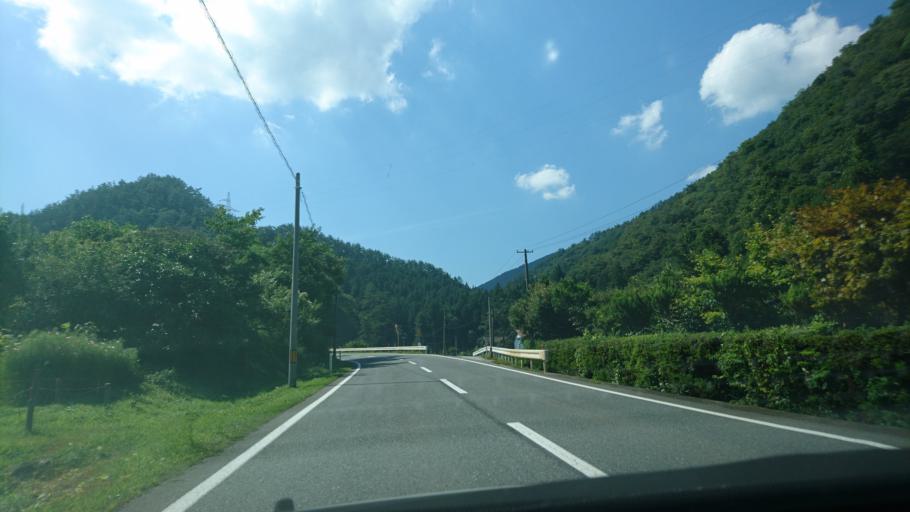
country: JP
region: Iwate
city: Ofunato
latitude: 39.0267
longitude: 141.5056
